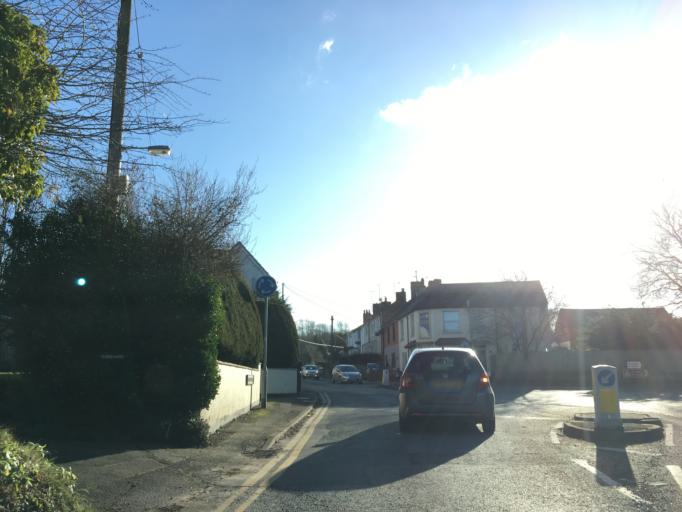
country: GB
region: England
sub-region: Borough of Swindon
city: Wroughton
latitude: 51.5248
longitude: -1.7872
